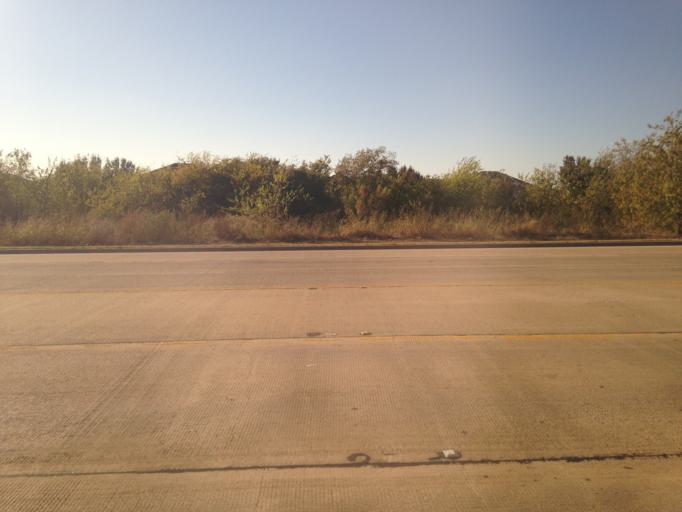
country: US
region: Texas
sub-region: Tarrant County
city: Watauga
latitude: 32.8667
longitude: -97.2631
